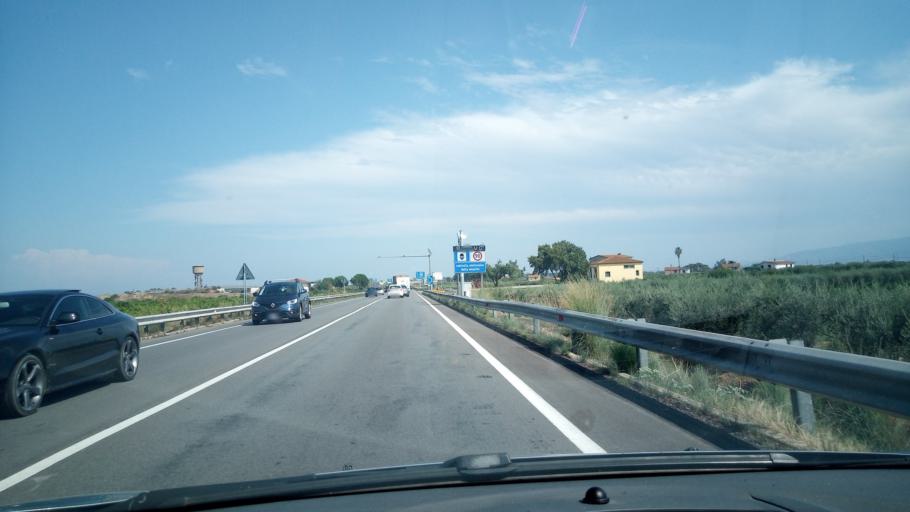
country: IT
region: Calabria
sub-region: Provincia di Cosenza
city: Sibari
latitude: 39.7236
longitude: 16.4390
